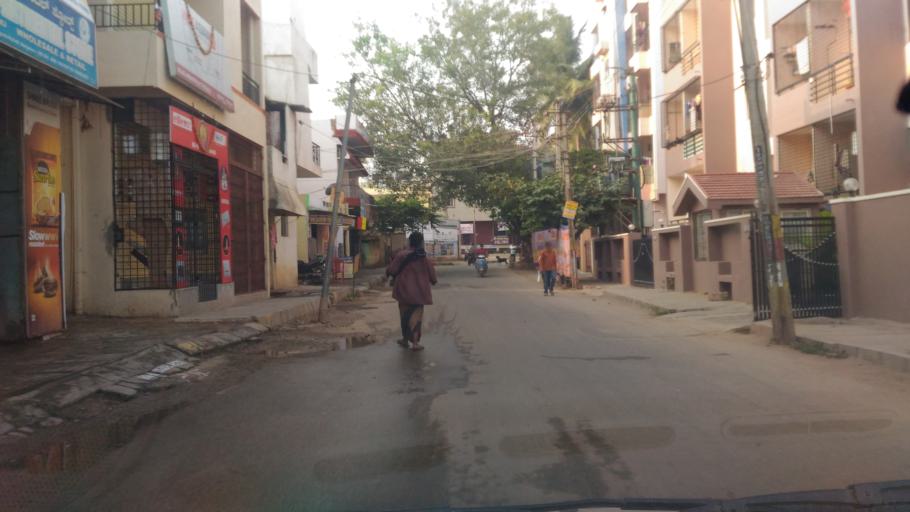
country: IN
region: Karnataka
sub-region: Bangalore Urban
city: Yelahanka
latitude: 13.0448
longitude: 77.5747
